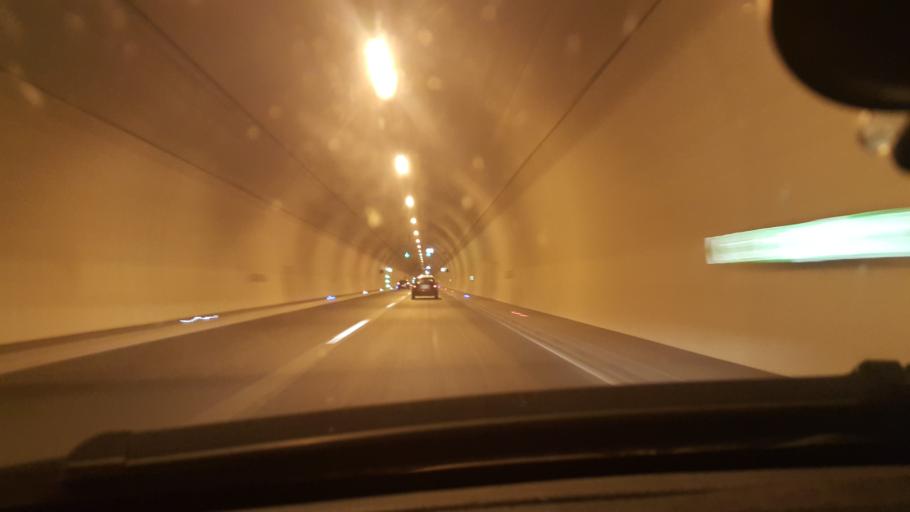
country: SI
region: Koper-Capodistria
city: Koper
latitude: 45.5402
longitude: 13.6993
